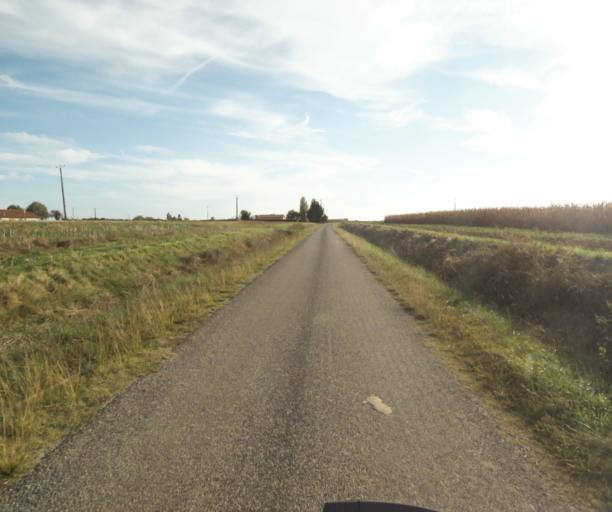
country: FR
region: Midi-Pyrenees
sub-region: Departement du Tarn-et-Garonne
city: Finhan
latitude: 43.9219
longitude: 1.1348
